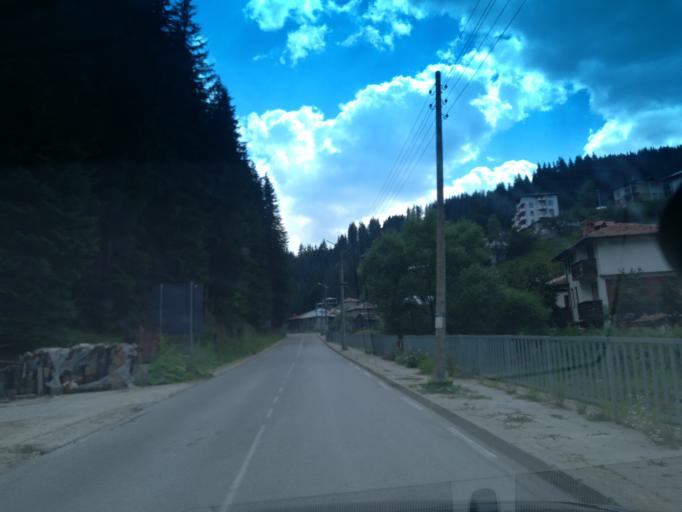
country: BG
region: Smolyan
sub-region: Obshtina Chepelare
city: Chepelare
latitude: 41.6626
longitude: 24.6351
